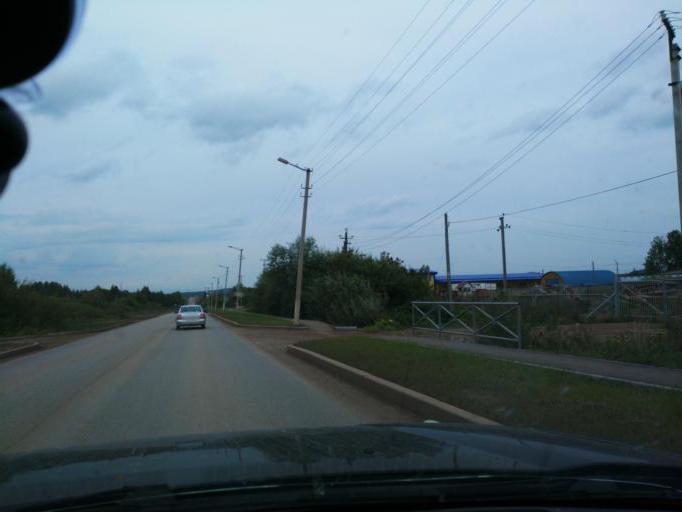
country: RU
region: Perm
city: Chernushka
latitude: 56.5374
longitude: 56.0988
